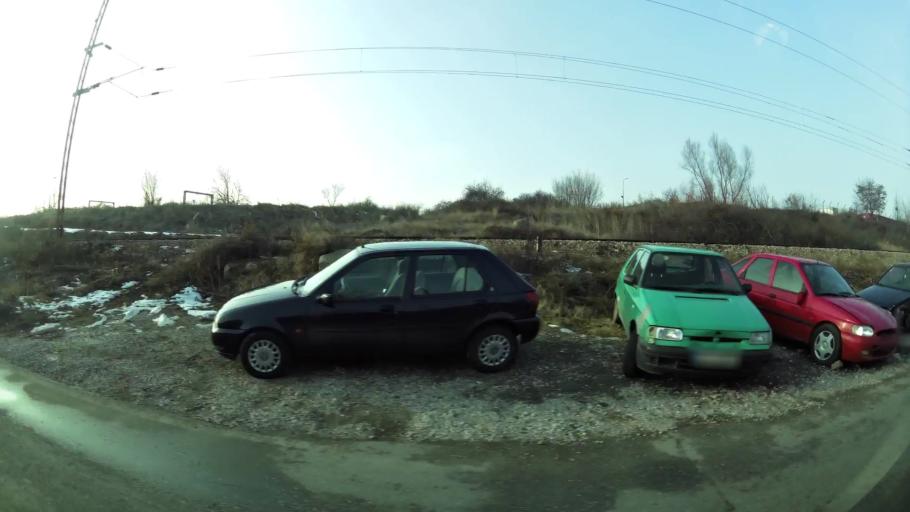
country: MK
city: Miladinovci
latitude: 41.9913
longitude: 21.6540
